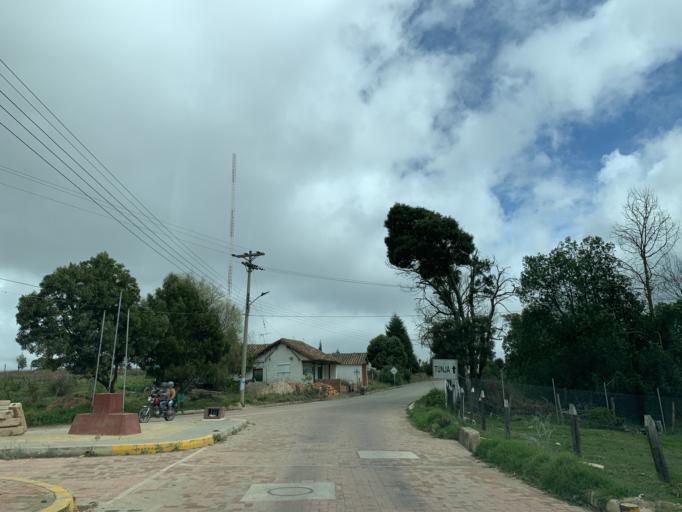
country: CO
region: Boyaca
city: Tunja
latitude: 5.5742
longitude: -73.3661
